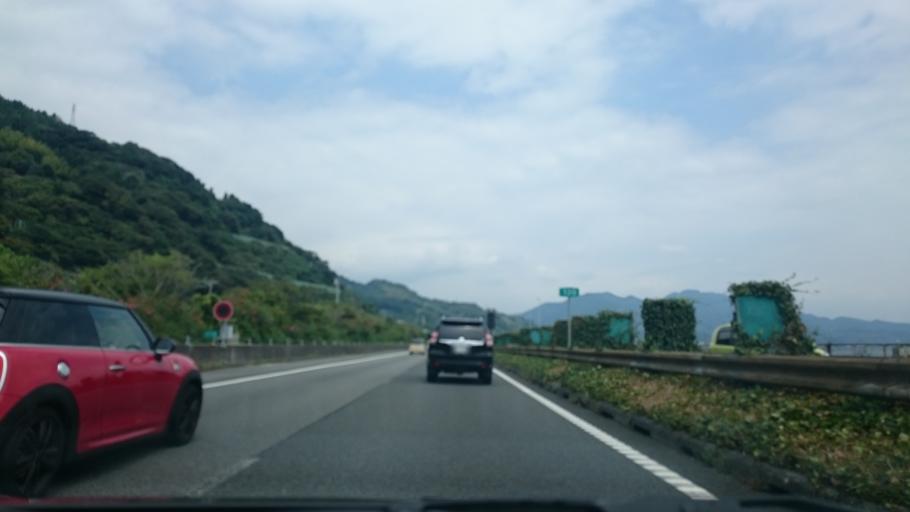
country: JP
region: Shizuoka
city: Fujinomiya
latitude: 35.0832
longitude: 138.5479
